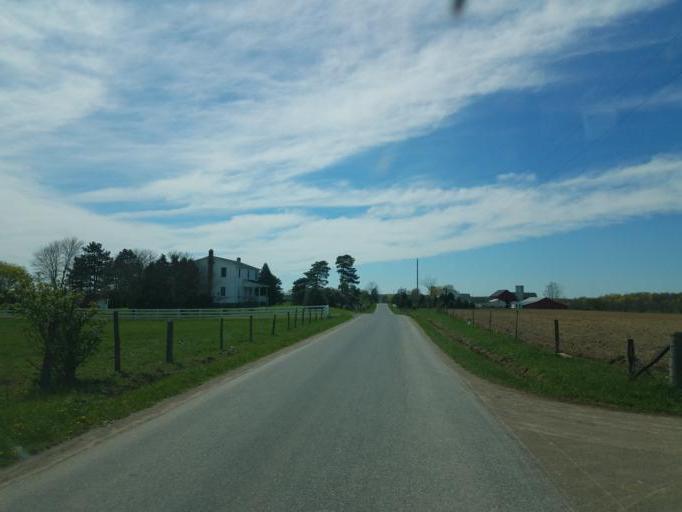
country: US
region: Ohio
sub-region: Ashland County
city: Ashland
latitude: 40.9166
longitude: -82.4137
